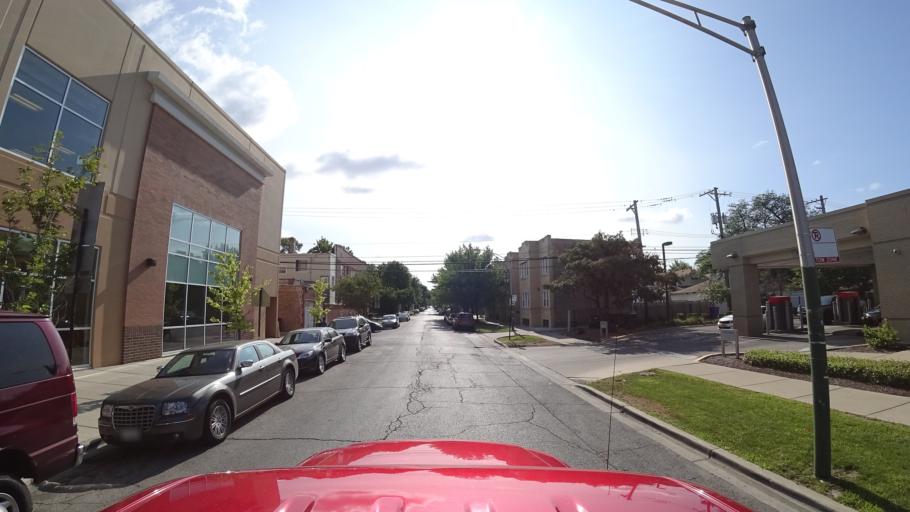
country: US
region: Illinois
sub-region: Cook County
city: Hometown
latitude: 41.7917
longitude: -87.7032
